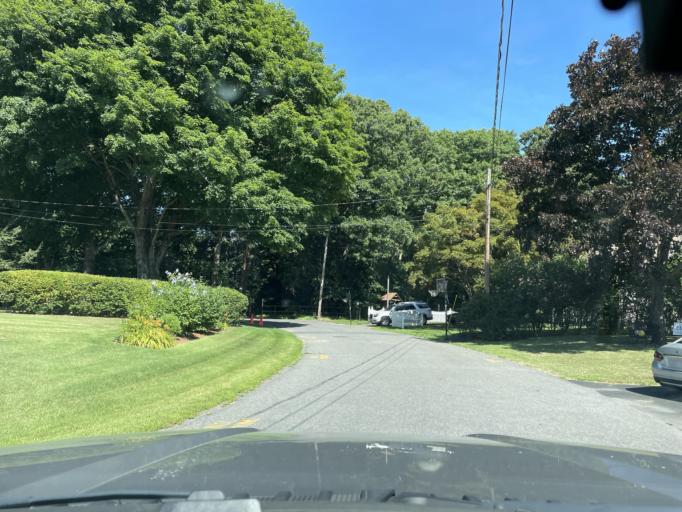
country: US
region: New York
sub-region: Ulster County
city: Saugerties South
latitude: 42.0651
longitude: -73.9605
